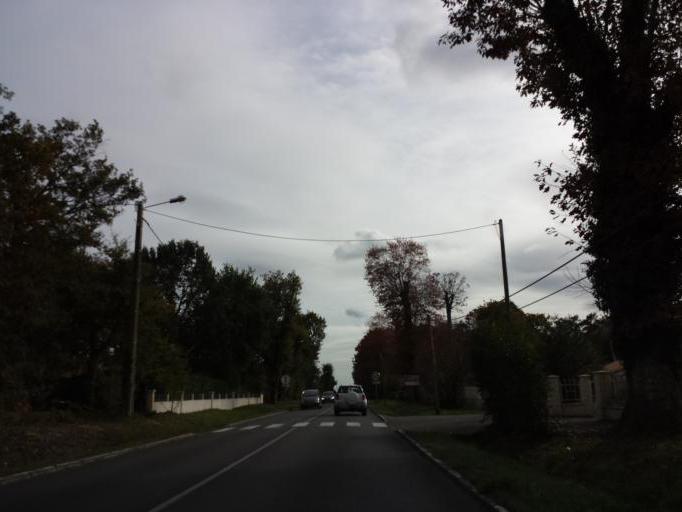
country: FR
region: Aquitaine
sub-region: Departement de la Gironde
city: Marcheprime
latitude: 44.7782
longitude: -0.9308
